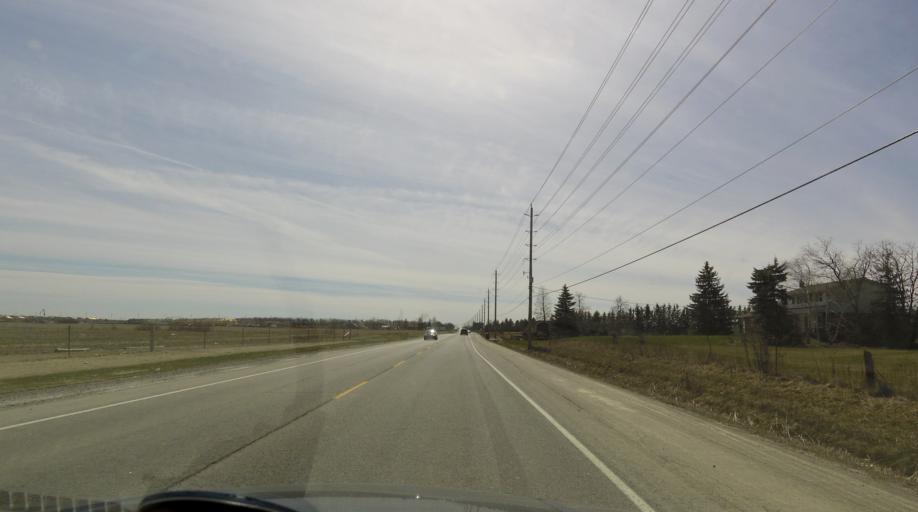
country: CA
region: Ontario
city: Brampton
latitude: 43.7105
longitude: -79.8502
